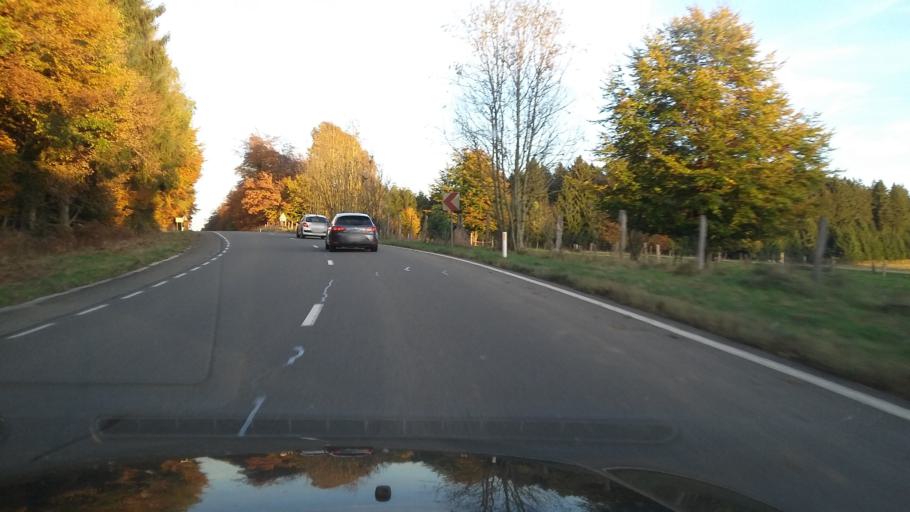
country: BE
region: Wallonia
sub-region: Province du Luxembourg
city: Herbeumont
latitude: 49.7532
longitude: 5.1634
